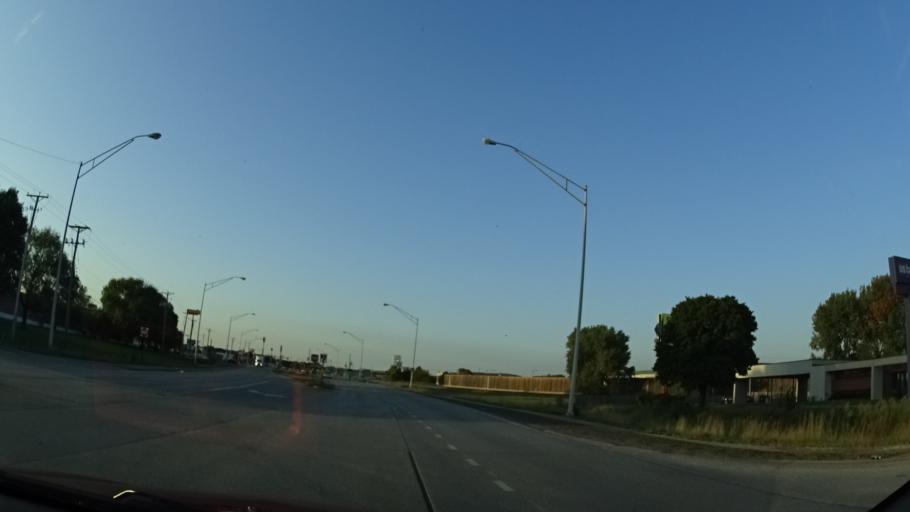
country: US
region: Iowa
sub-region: Pottawattamie County
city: Council Bluffs
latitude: 41.2252
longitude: -95.8507
